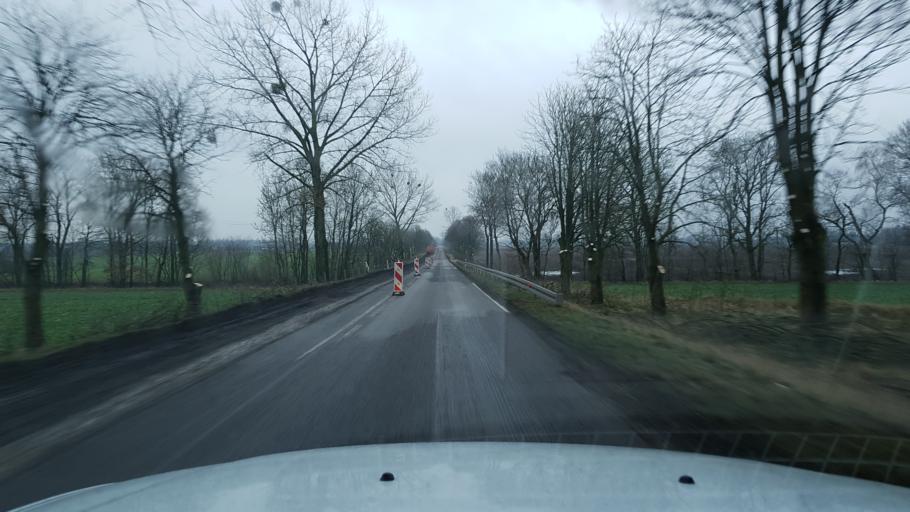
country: PL
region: West Pomeranian Voivodeship
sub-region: Powiat gryficki
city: Ploty
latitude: 53.8306
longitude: 15.2447
